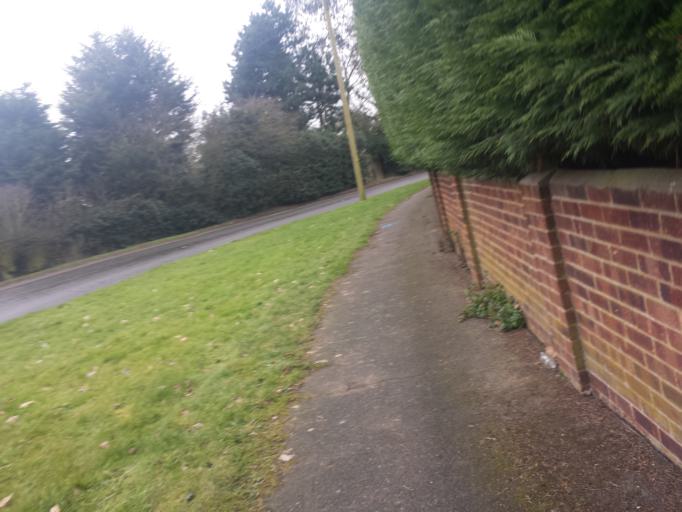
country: GB
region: England
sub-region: Essex
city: Little Clacton
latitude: 51.8988
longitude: 1.1853
